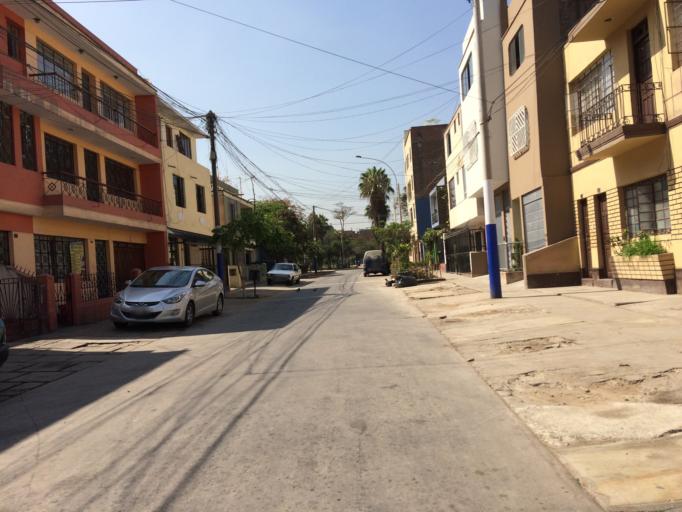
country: PE
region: Lima
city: Lima
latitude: -12.0259
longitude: -77.0381
